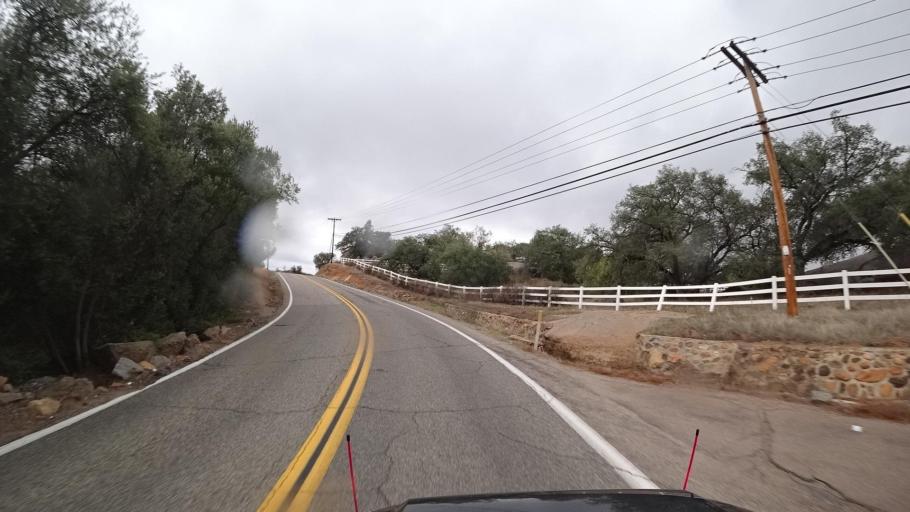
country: US
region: California
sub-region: San Diego County
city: Alpine
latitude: 32.8268
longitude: -116.7569
